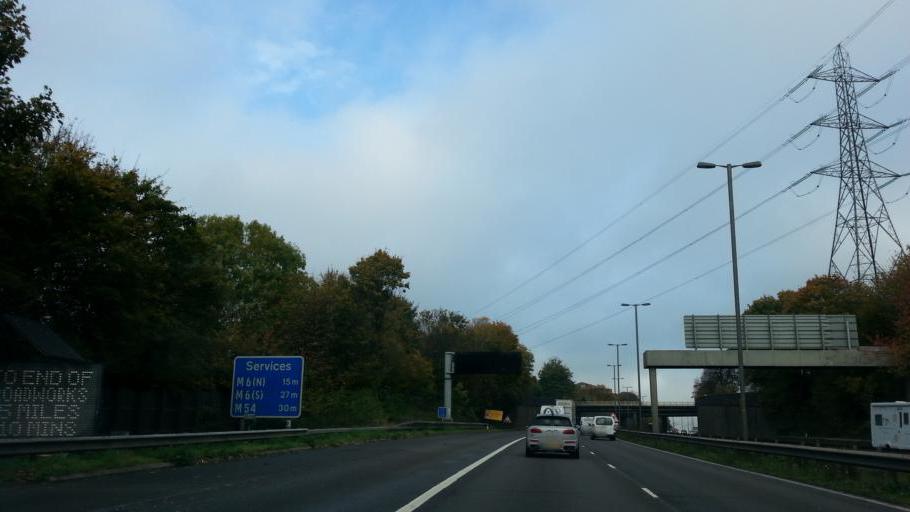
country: GB
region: England
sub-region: City and Borough of Birmingham
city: Bartley Green
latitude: 52.4592
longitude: -2.0131
